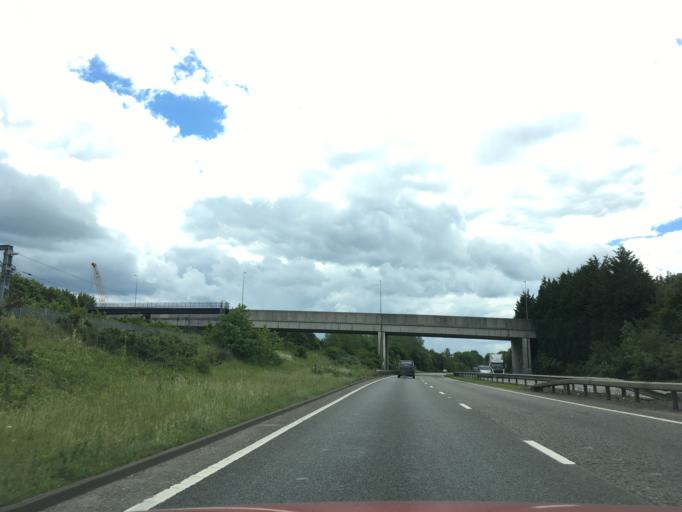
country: GB
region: England
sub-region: Milton Keynes
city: Milton Keynes
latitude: 52.0242
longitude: -0.7625
